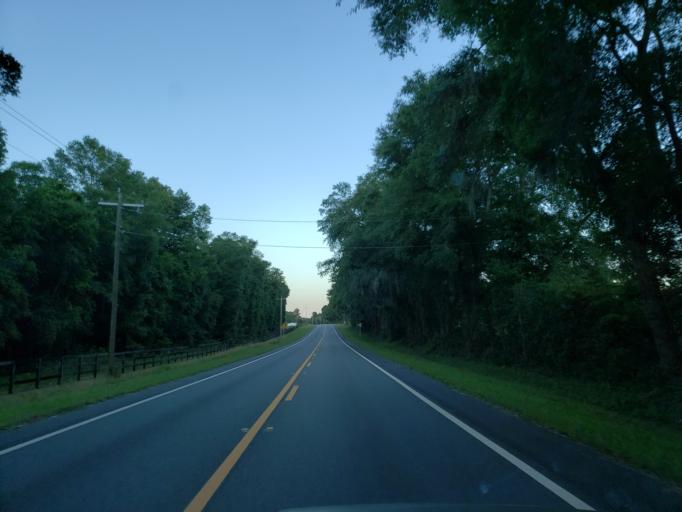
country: US
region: Georgia
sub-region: Echols County
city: Statenville
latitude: 30.5811
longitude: -83.1973
